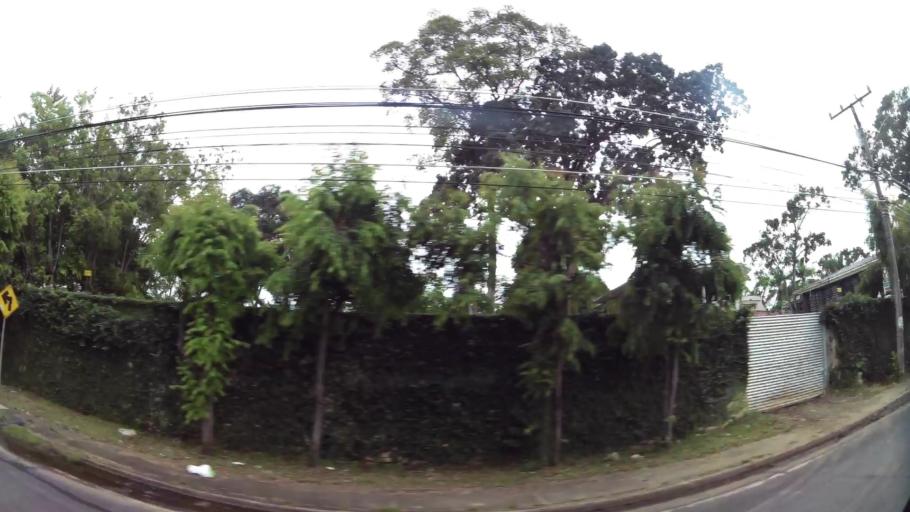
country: PA
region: Panama
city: Panama
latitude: 8.9994
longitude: -79.5019
